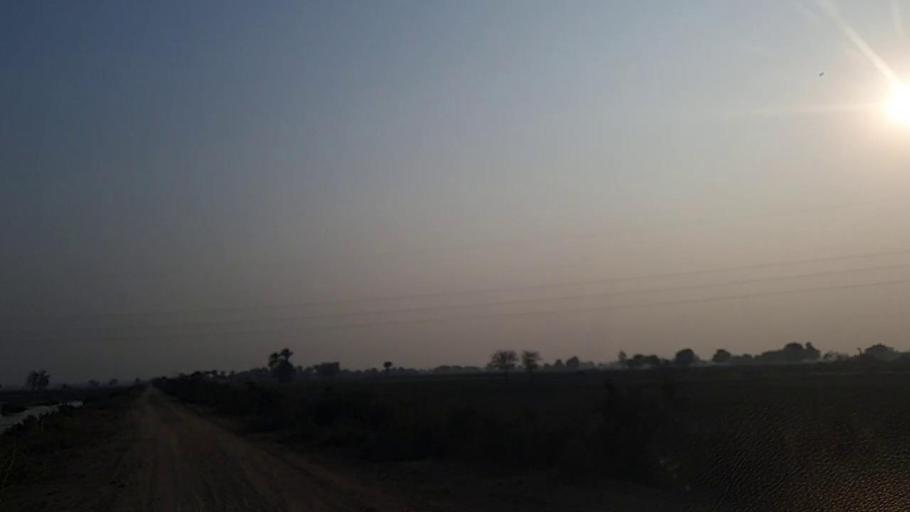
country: PK
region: Sindh
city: Nawabshah
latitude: 26.2358
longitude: 68.4678
